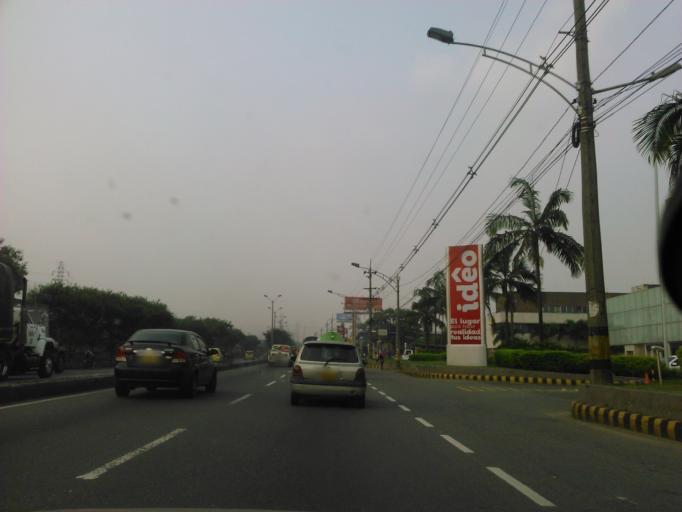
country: CO
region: Antioquia
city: Envigado
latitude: 6.1826
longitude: -75.5902
